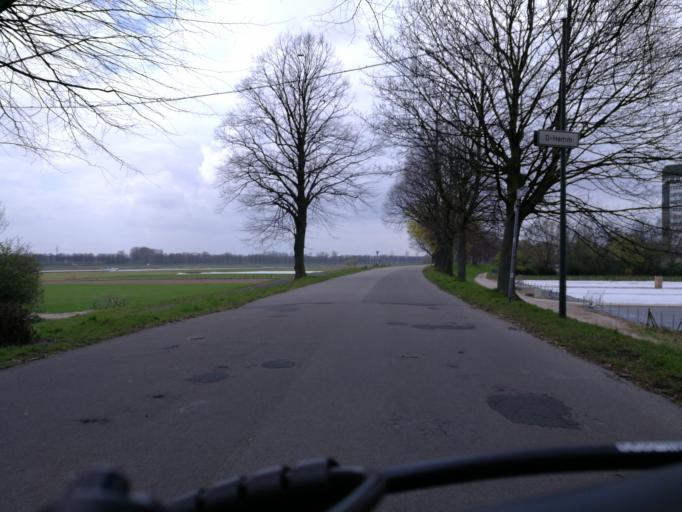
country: DE
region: North Rhine-Westphalia
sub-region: Regierungsbezirk Dusseldorf
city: Dusseldorf
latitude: 51.1863
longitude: 6.7420
